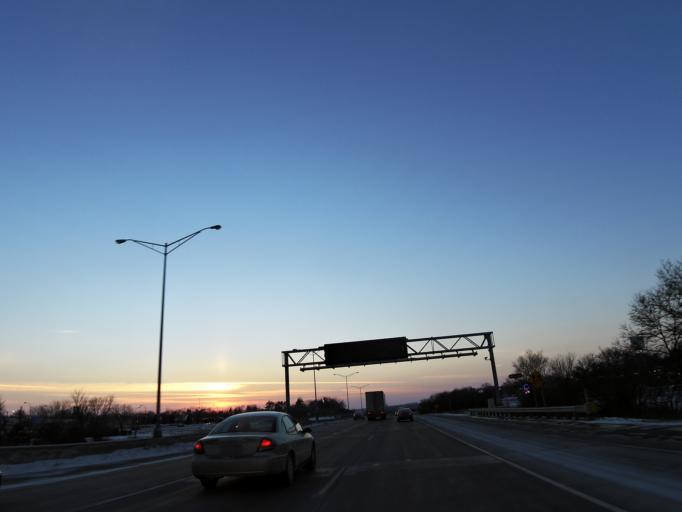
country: US
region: Wisconsin
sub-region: Saint Croix County
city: Hudson
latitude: 44.9630
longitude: -92.7380
